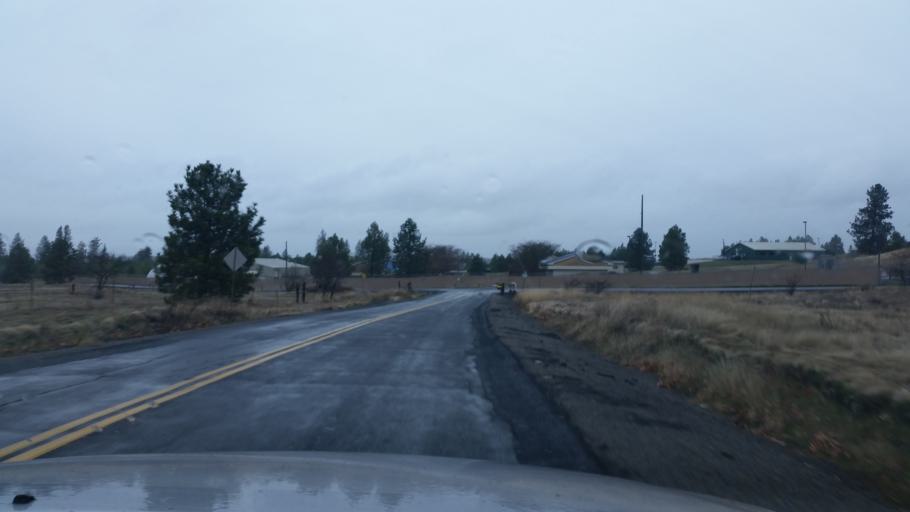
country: US
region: Washington
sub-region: Spokane County
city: Airway Heights
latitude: 47.7002
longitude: -117.5757
